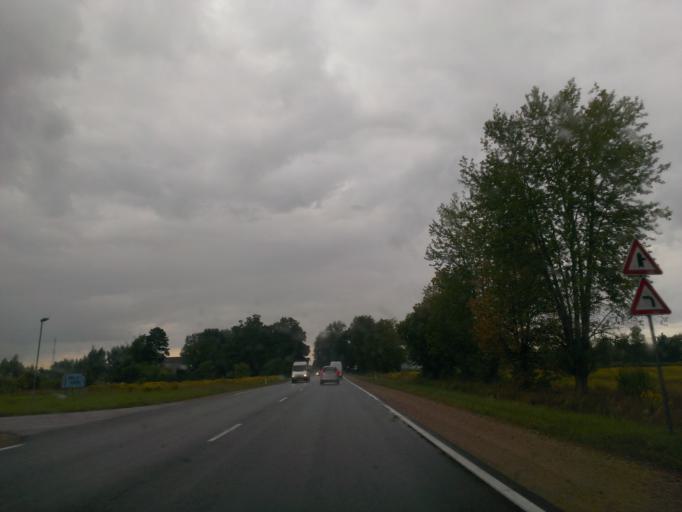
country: LV
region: Kegums
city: Kegums
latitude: 56.7683
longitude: 24.6764
